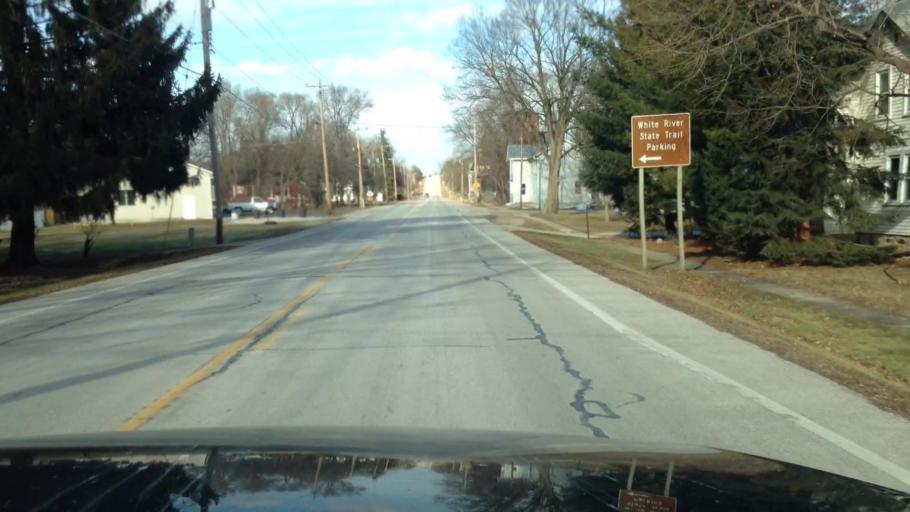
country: US
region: Wisconsin
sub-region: Walworth County
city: Lake Geneva
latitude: 42.6418
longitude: -88.4136
